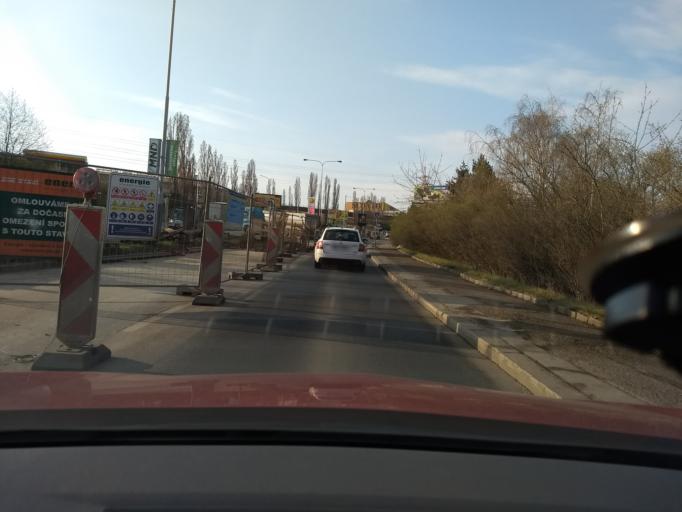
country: CZ
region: Central Bohemia
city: Hostivice
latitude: 50.0592
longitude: 14.3112
